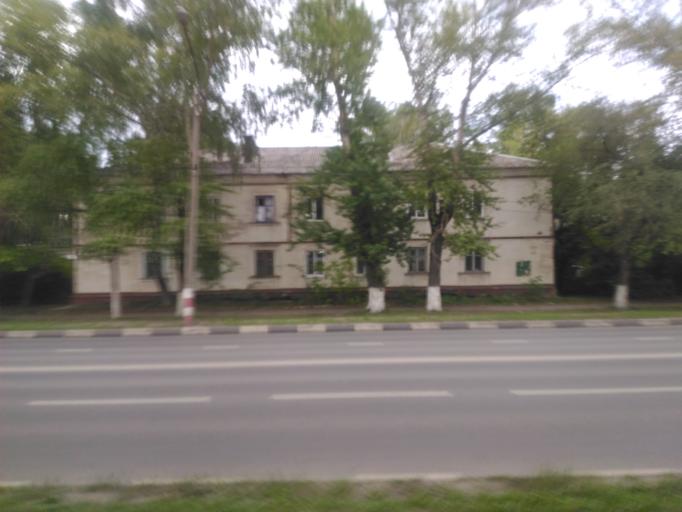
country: RU
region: Ulyanovsk
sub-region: Ulyanovskiy Rayon
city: Ulyanovsk
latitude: 54.2762
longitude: 48.3369
